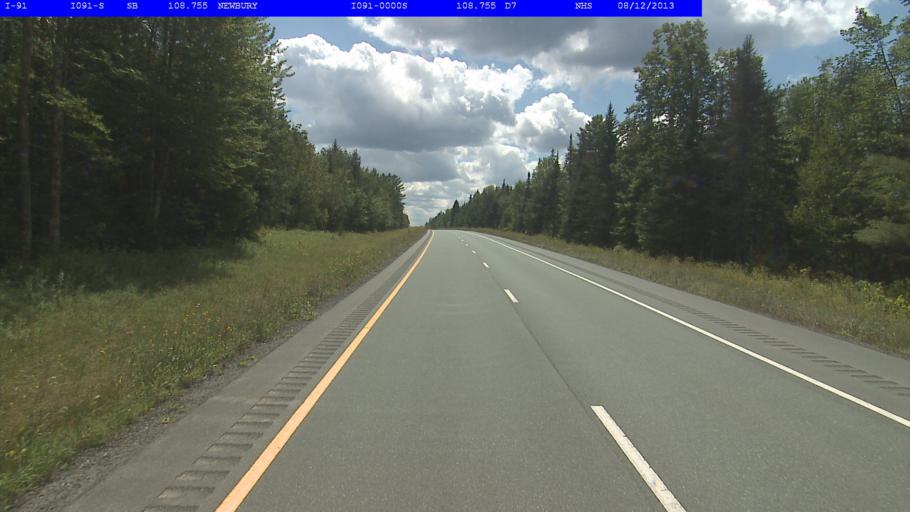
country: US
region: New Hampshire
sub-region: Grafton County
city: Woodsville
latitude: 44.1396
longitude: -72.1027
